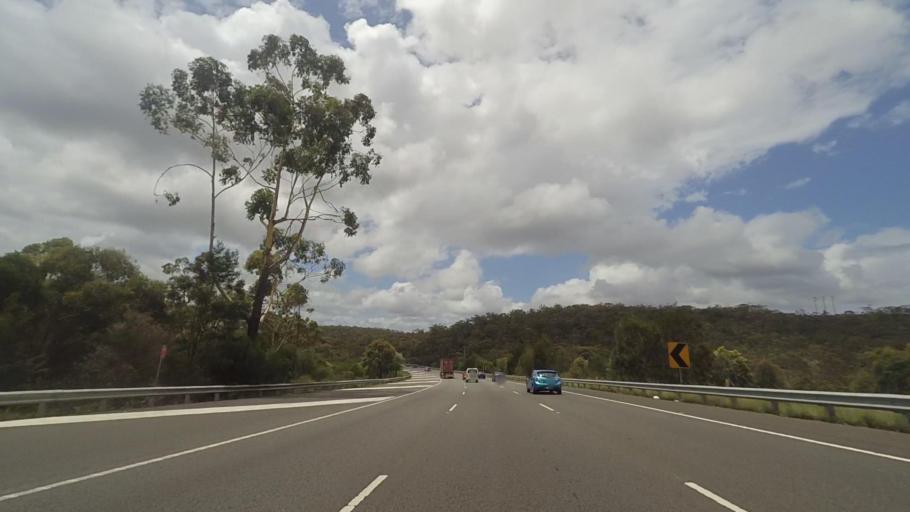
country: AU
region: New South Wales
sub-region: Gosford Shire
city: Point Clare
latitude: -33.4494
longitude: 151.2172
